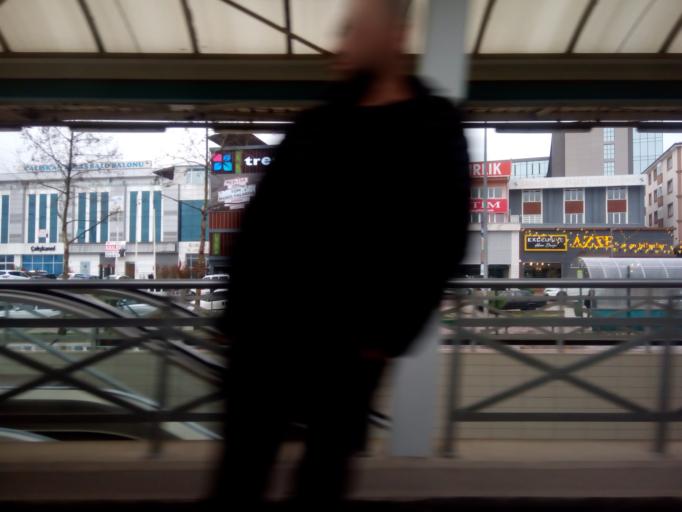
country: TR
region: Bursa
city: Niluefer
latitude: 40.2372
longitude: 28.9754
